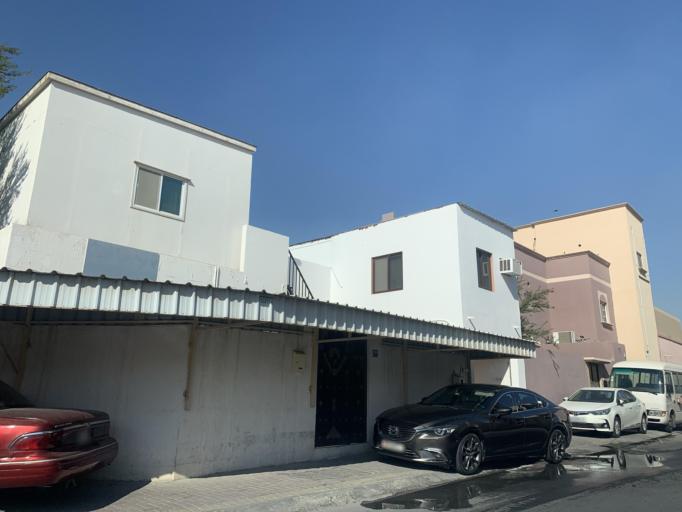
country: BH
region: Central Governorate
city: Madinat Hamad
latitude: 26.1153
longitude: 50.5080
